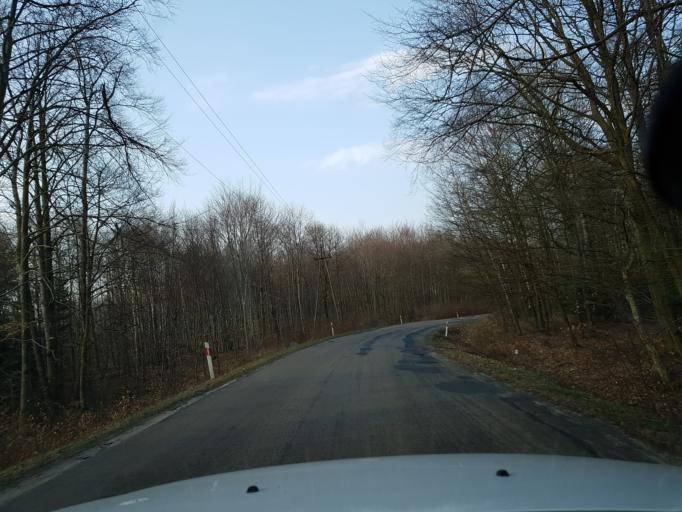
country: PL
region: West Pomeranian Voivodeship
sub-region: Powiat swidwinski
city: Polczyn-Zdroj
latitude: 53.7353
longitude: 16.0759
